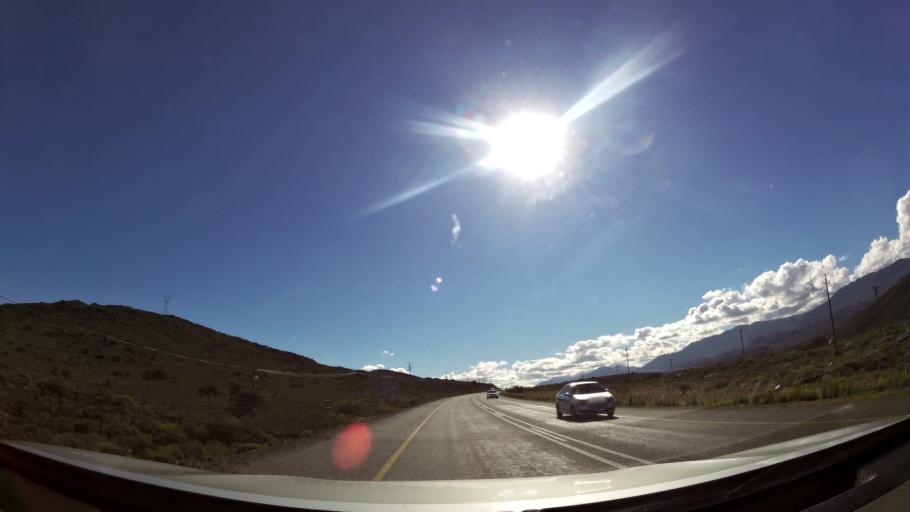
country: ZA
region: Western Cape
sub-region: Cape Winelands District Municipality
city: Ashton
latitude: -33.7887
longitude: 19.7749
